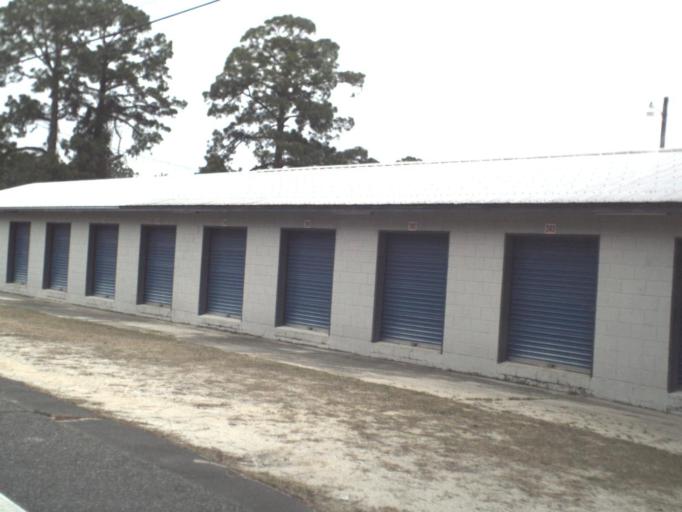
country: US
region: Florida
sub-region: Bay County
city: Parker
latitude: 30.1301
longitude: -85.5941
